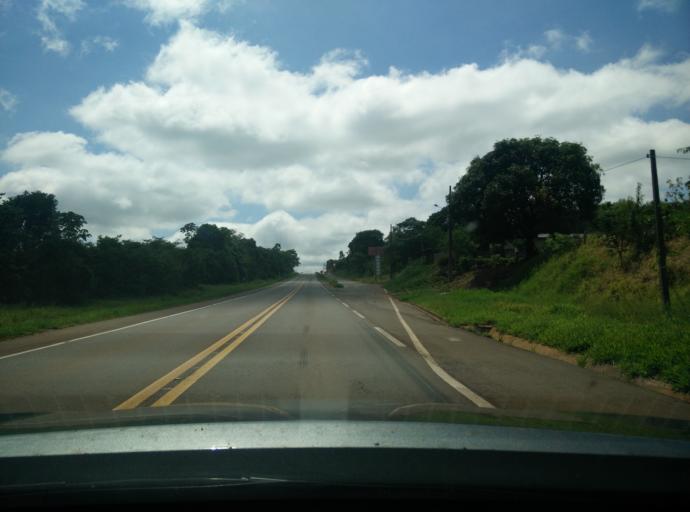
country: BR
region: Parana
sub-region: Campo Mourao
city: Campo Mourao
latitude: -23.9711
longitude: -52.5609
